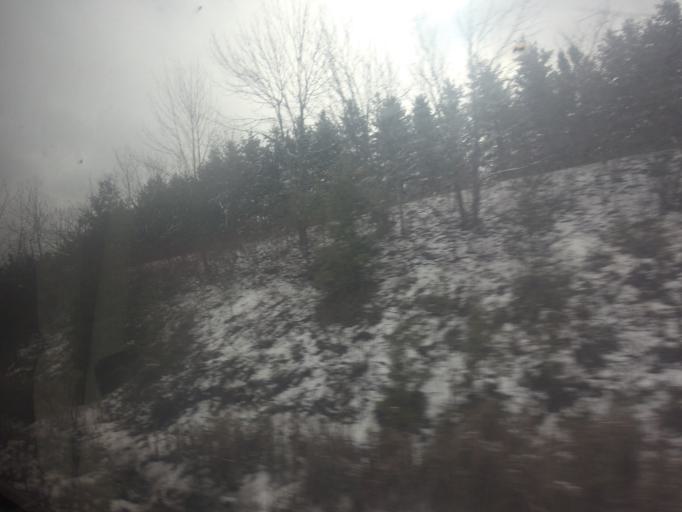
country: CA
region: Ontario
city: Cobourg
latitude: 43.9469
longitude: -78.3743
